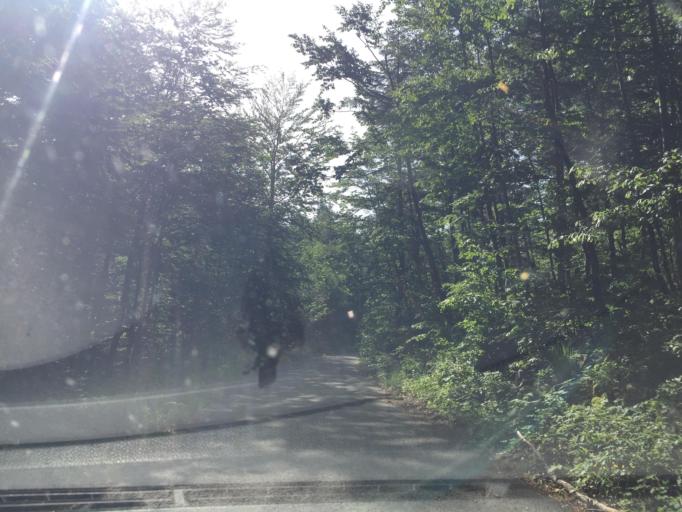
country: HR
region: Primorsko-Goranska
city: Podhum
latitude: 45.4208
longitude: 14.5721
